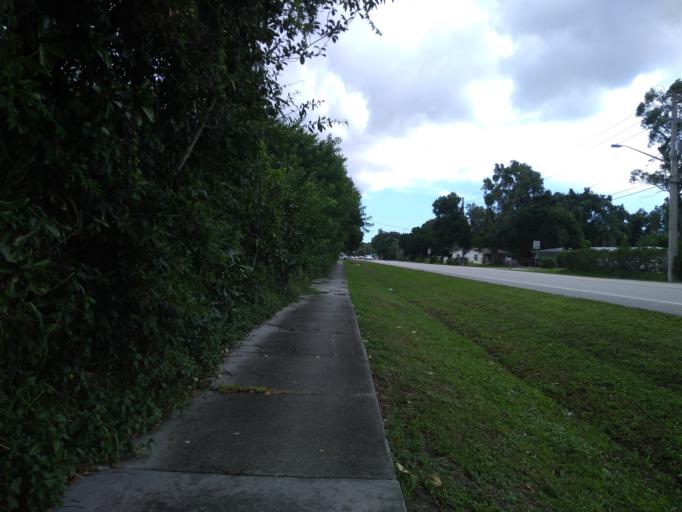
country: US
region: Florida
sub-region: Indian River County
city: Vero Beach
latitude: 27.6348
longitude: -80.4139
